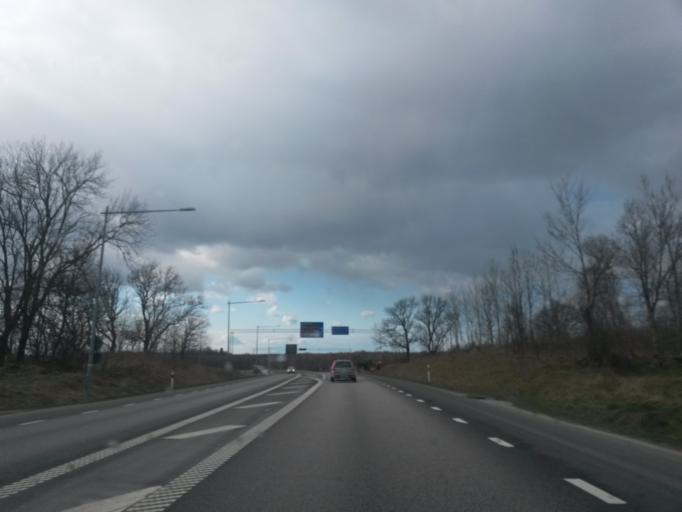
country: SE
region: Vaestra Goetaland
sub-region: Skara Kommun
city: Axvall
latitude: 58.3892
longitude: 13.6528
